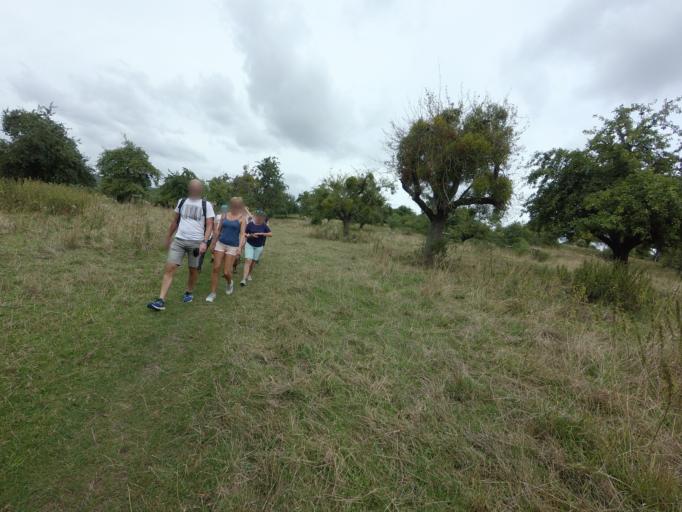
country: BE
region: Wallonia
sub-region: Province de Liege
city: Plombieres
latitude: 50.7644
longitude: 5.9362
